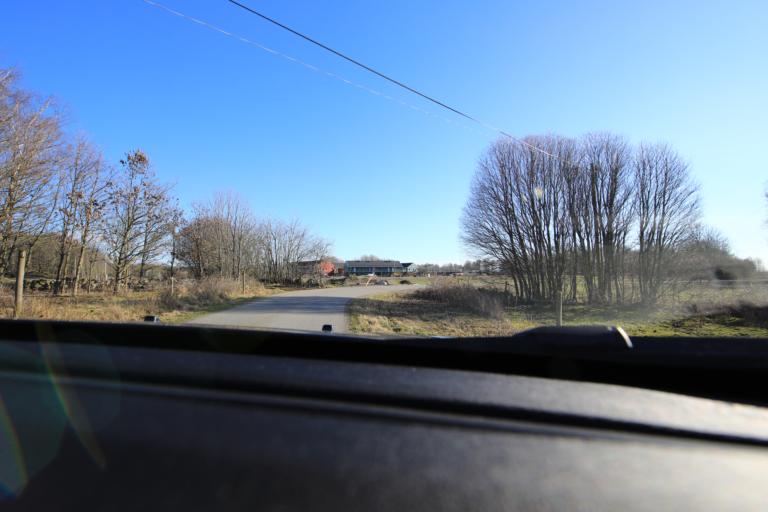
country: SE
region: Halland
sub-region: Varbergs Kommun
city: Tvaaker
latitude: 57.0503
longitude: 12.3770
